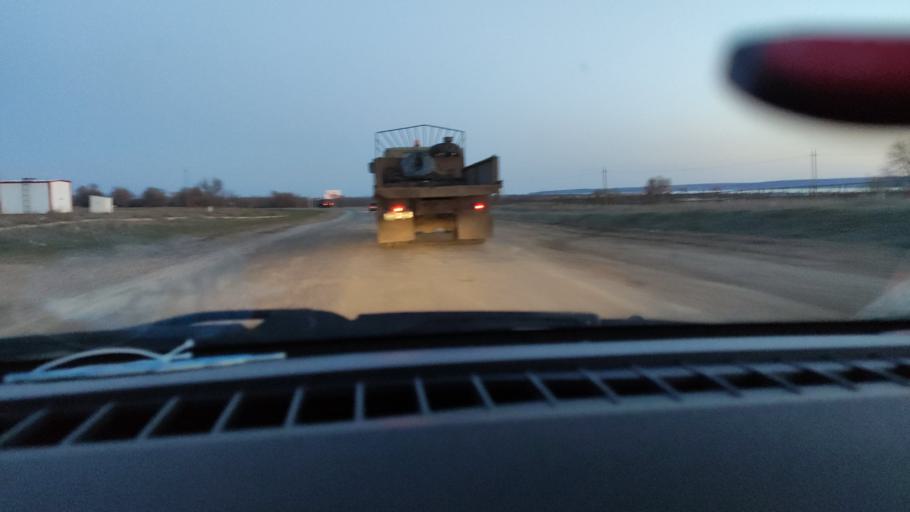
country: RU
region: Saratov
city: Rovnoye
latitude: 51.0171
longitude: 46.0948
